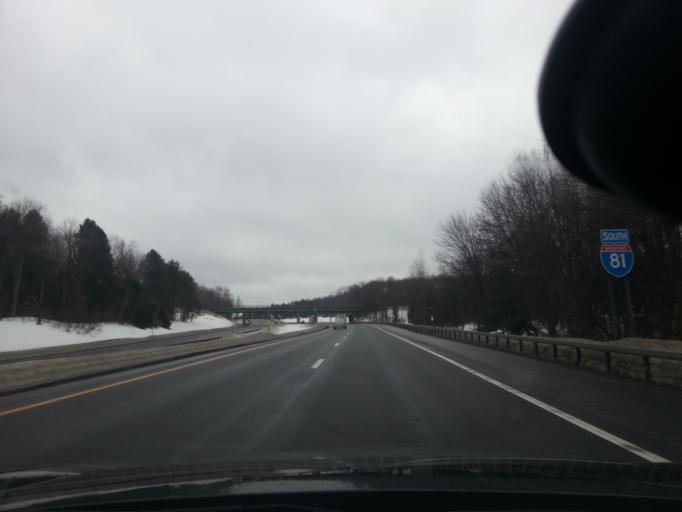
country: US
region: New York
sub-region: Oswego County
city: Central Square
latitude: 43.3759
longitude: -76.1221
